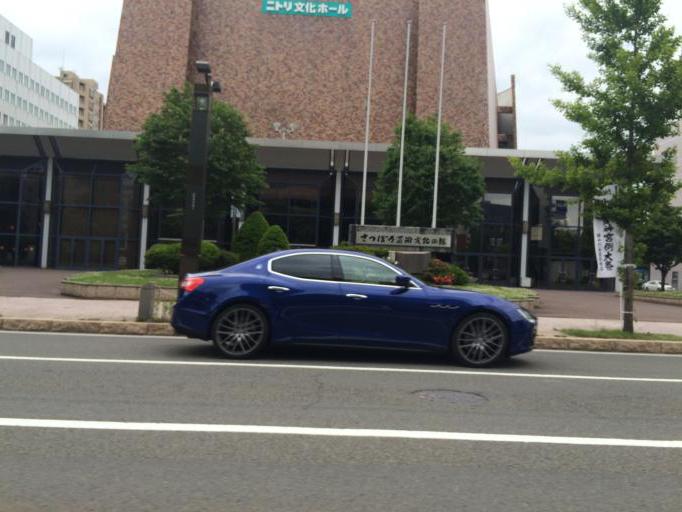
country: JP
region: Hokkaido
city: Sapporo
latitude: 43.0603
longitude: 141.3387
